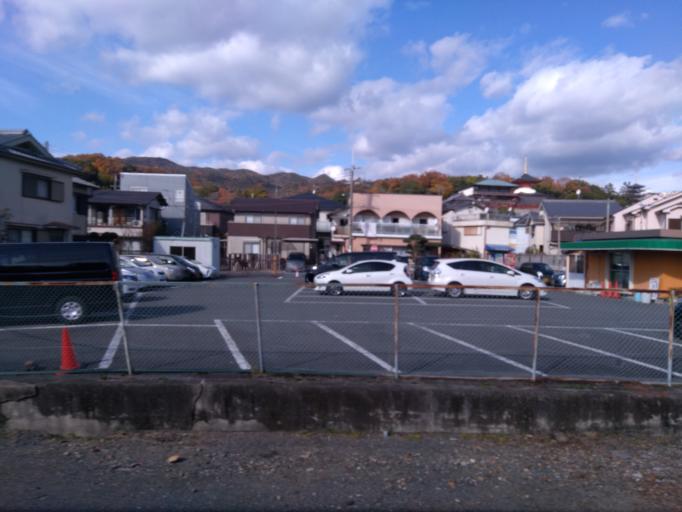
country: JP
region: Hyogo
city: Takarazuka
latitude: 34.8186
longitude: 135.3674
